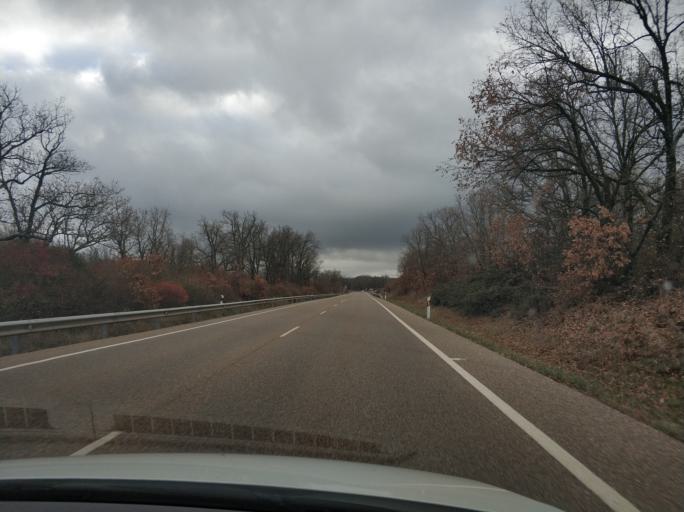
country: ES
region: Castille and Leon
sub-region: Provincia de Segovia
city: Riaza
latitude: 41.3051
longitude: -3.4778
